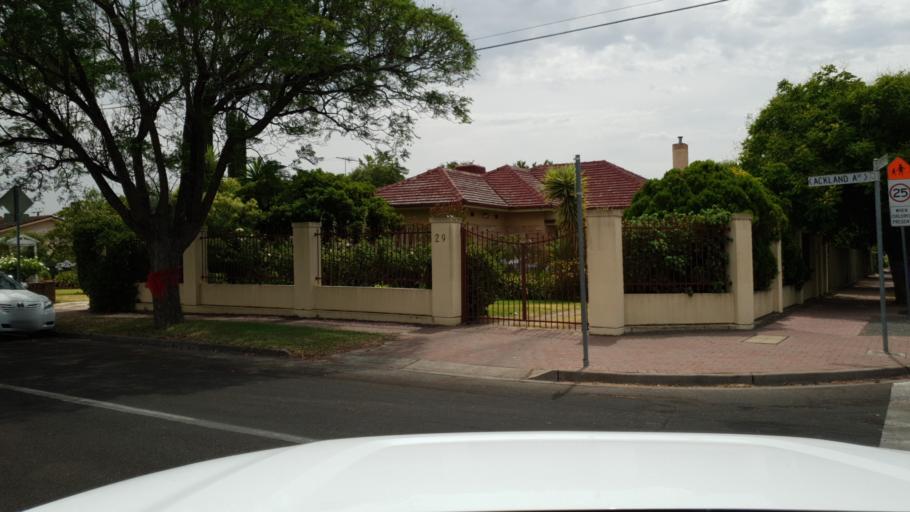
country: AU
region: South Australia
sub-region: Mitcham
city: Clarence Gardens
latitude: -34.9701
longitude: 138.5796
